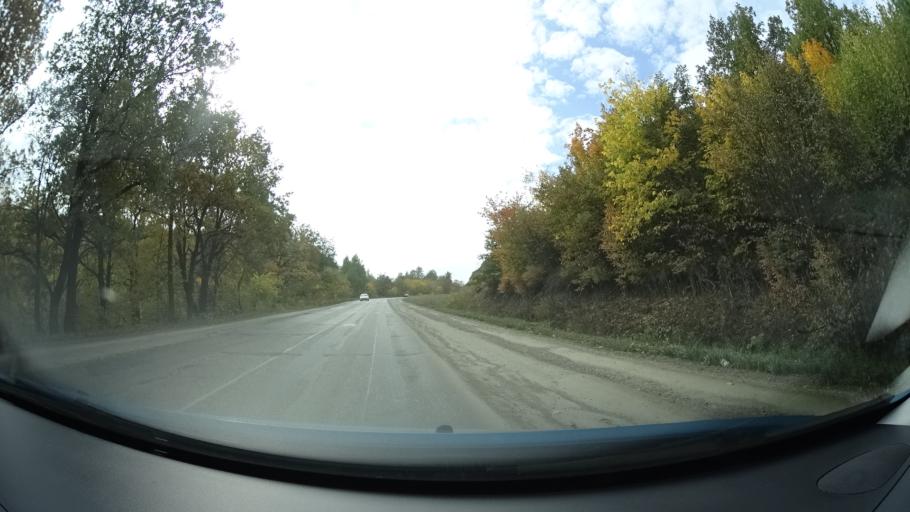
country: RU
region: Tatarstan
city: Urussu
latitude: 54.5492
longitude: 53.5823
